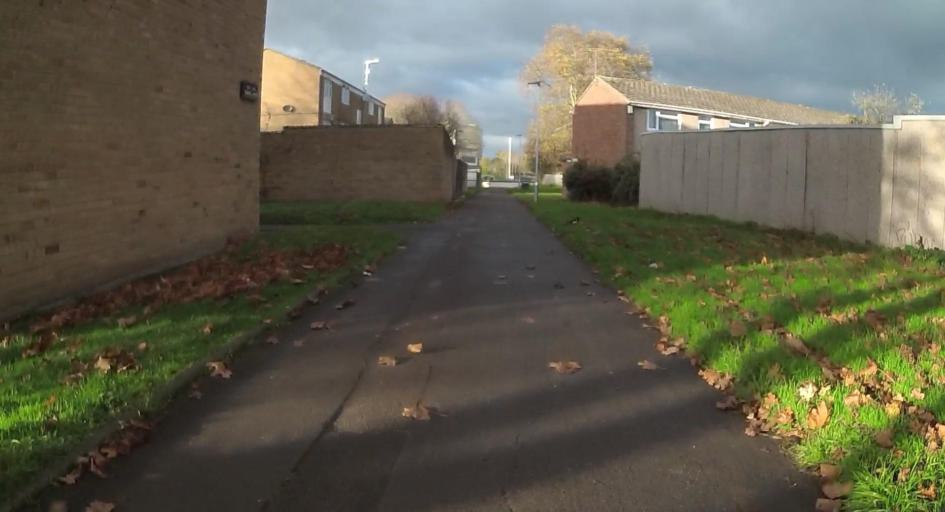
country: GB
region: England
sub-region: Bracknell Forest
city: Bracknell
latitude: 51.4024
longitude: -0.7715
